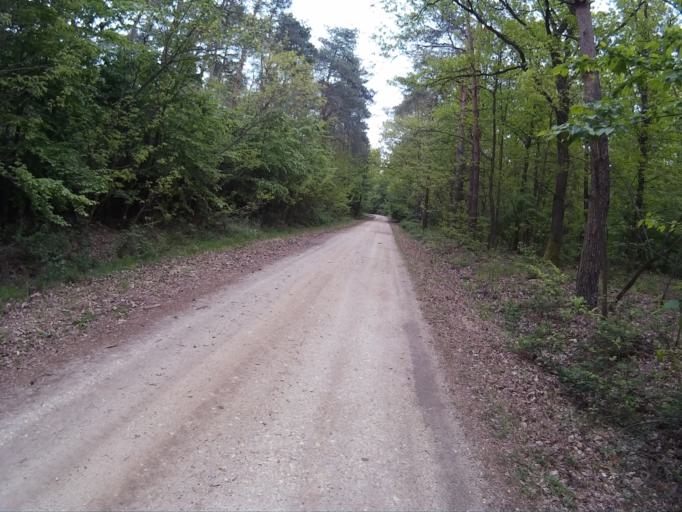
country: HU
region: Vas
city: Vasvar
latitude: 47.0670
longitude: 16.8865
